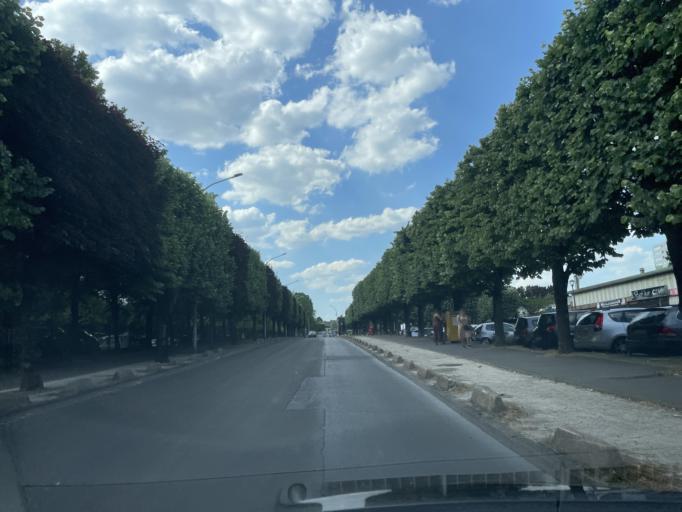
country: FR
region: Ile-de-France
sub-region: Departement du Val-de-Marne
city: Bonneuil-sur-Marne
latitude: 48.7695
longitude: 2.4815
